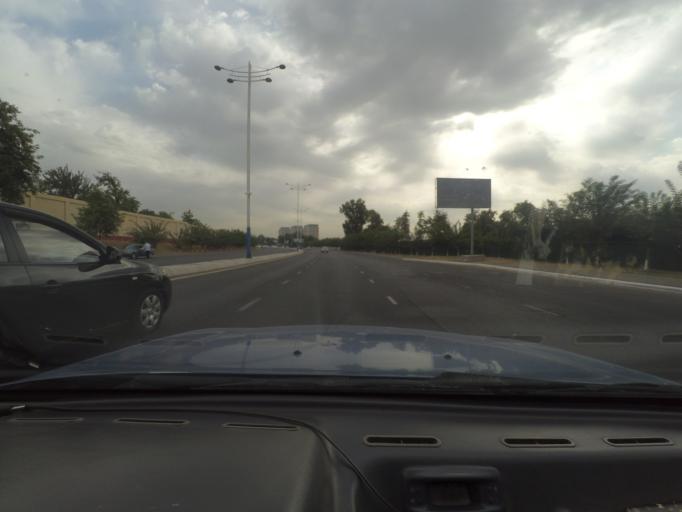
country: UZ
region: Toshkent
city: Salor
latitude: 41.3544
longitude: 69.3739
